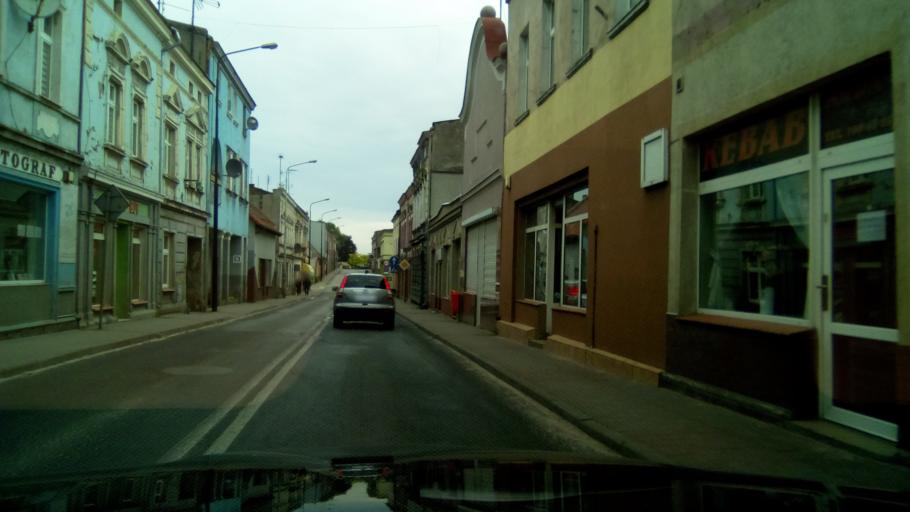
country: PL
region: Kujawsko-Pomorskie
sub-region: Powiat sepolenski
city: Wiecbork
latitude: 53.3495
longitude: 17.4864
